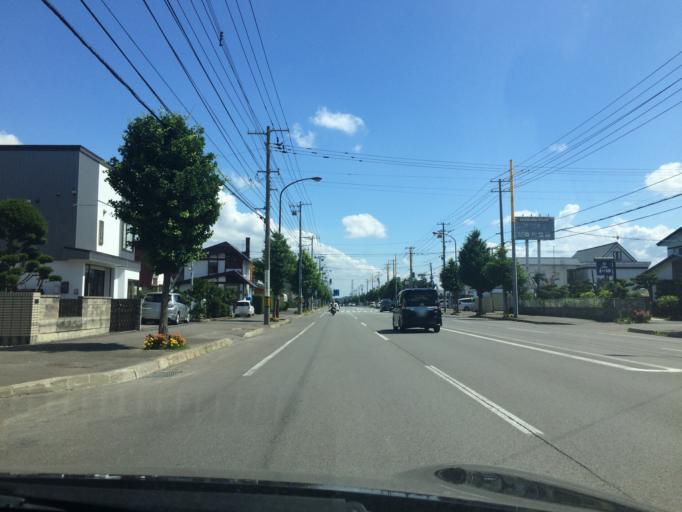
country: JP
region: Hokkaido
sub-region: Asahikawa-shi
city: Asahikawa
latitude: 43.7498
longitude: 142.3410
